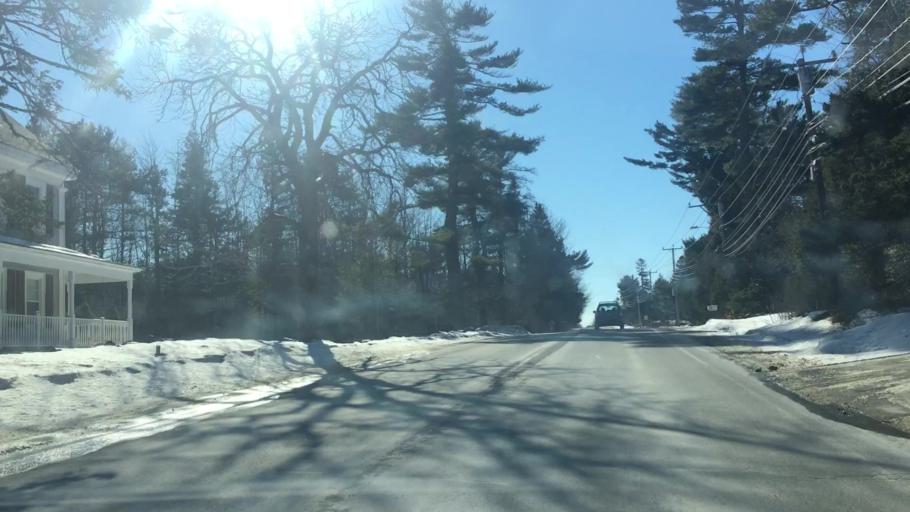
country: US
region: Maine
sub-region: Hancock County
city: Ellsworth
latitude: 44.5194
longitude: -68.4313
